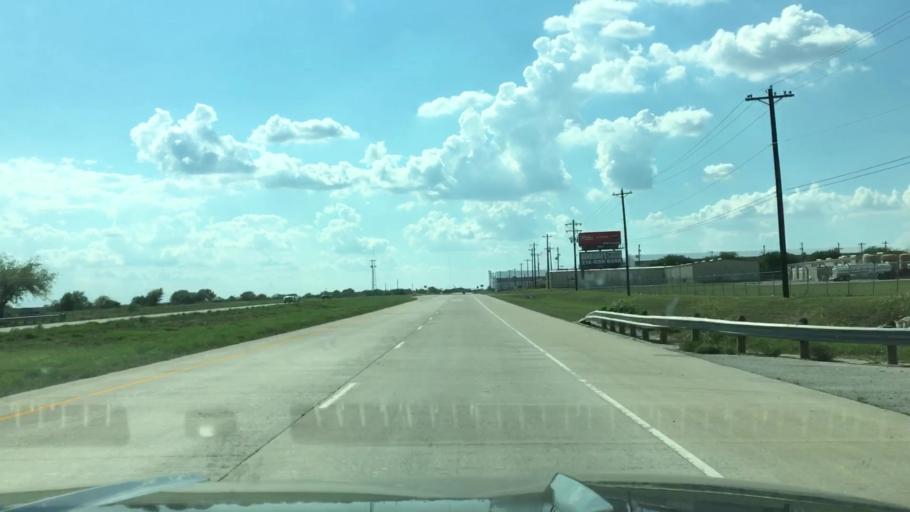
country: US
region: Texas
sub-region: Tarrant County
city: Haslet
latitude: 33.0360
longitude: -97.3827
